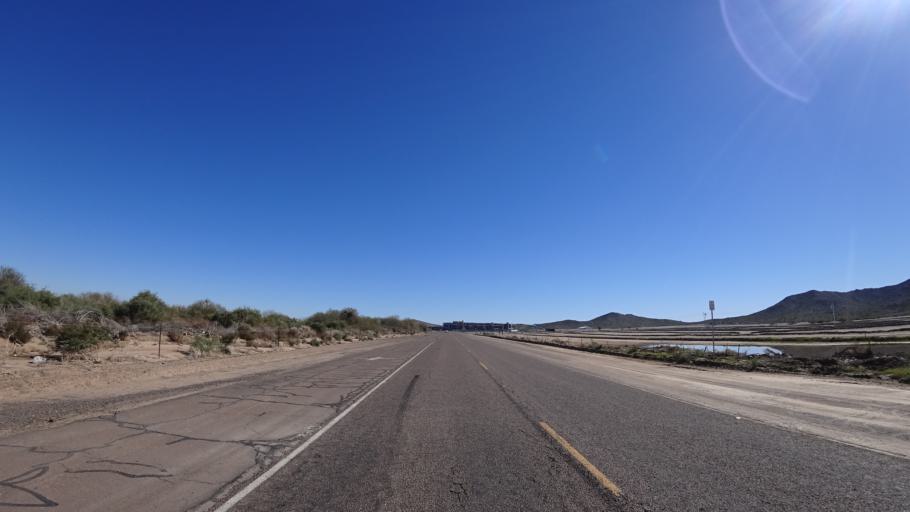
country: US
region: Arizona
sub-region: Maricopa County
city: Avondale
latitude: 33.3756
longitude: -112.3295
